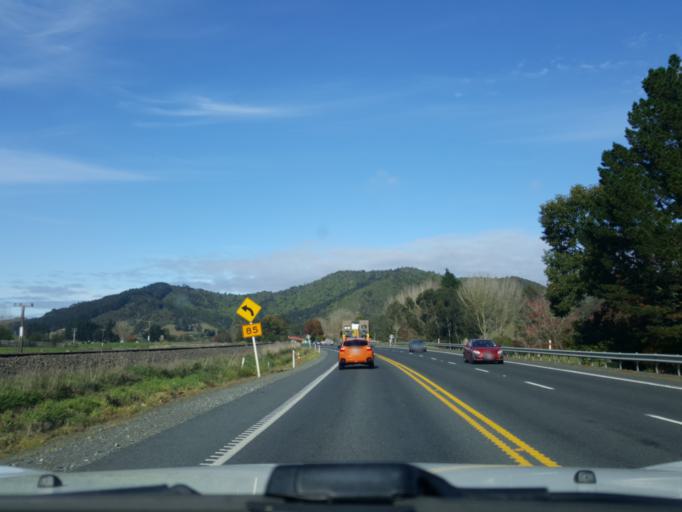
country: NZ
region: Waikato
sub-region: Waikato District
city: Ngaruawahia
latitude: -37.5902
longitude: 175.1594
